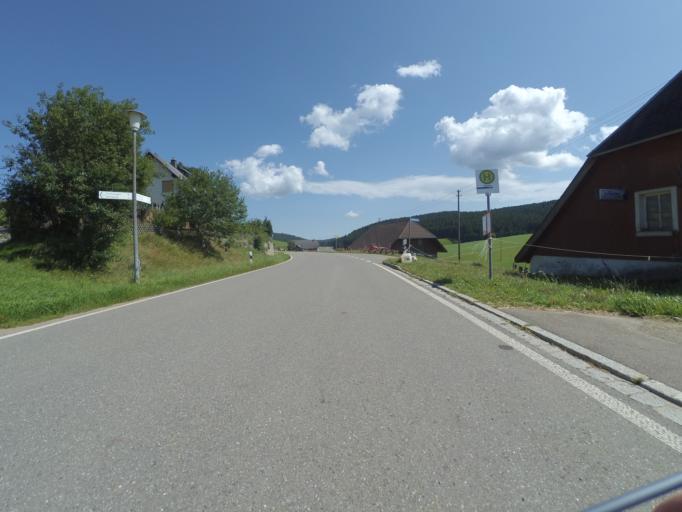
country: DE
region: Baden-Wuerttemberg
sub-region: Freiburg Region
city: Eisenbach
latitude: 47.9843
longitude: 8.2493
